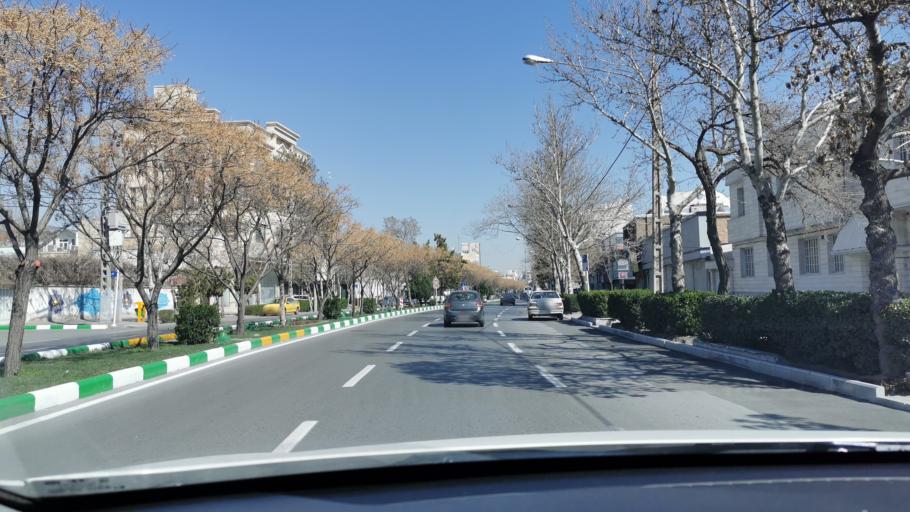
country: IR
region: Razavi Khorasan
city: Mashhad
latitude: 36.2936
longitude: 59.5723
